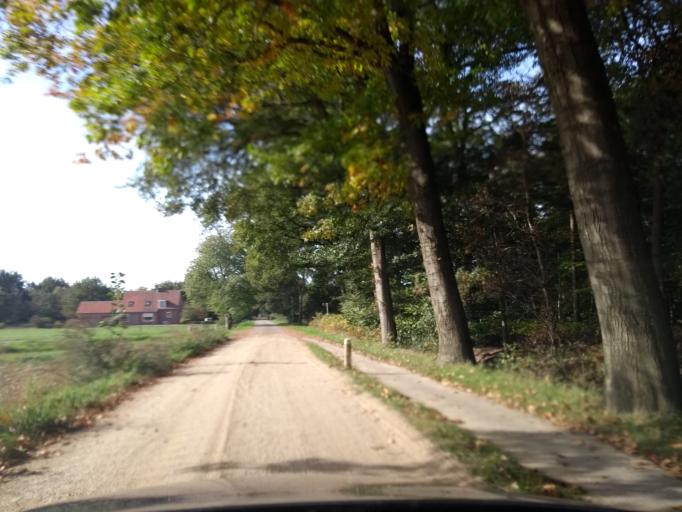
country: NL
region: Gelderland
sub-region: Gemeente Bronckhorst
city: Zelhem
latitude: 52.0407
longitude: 6.3503
